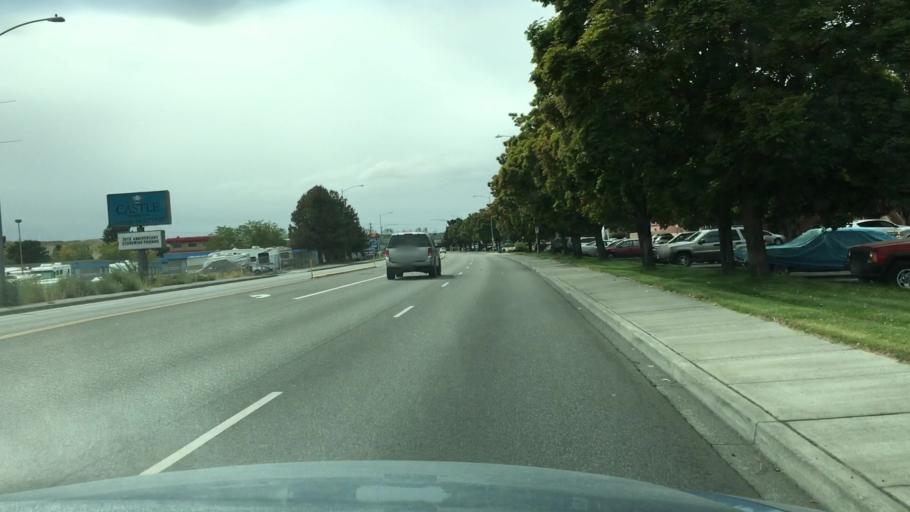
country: US
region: Washington
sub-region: Franklin County
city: West Pasco
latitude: 46.2154
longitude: -119.2253
